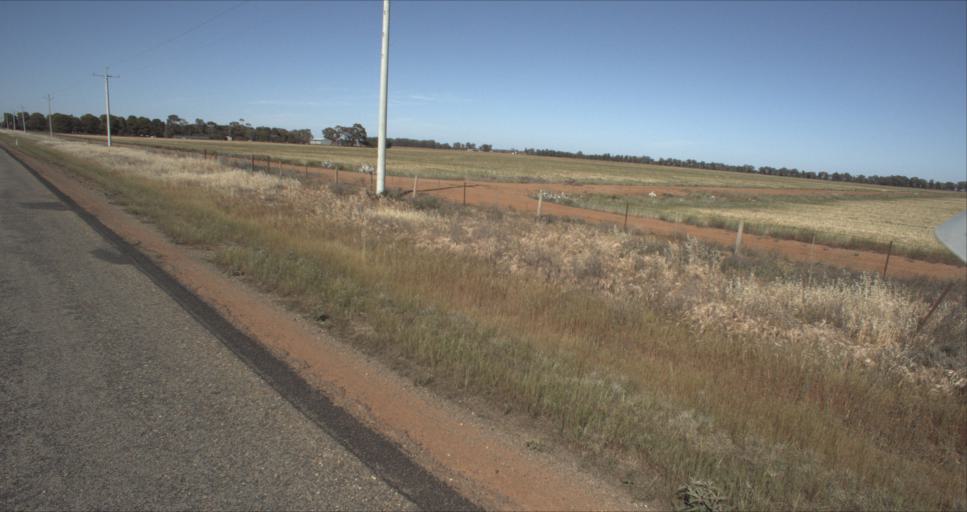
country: AU
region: New South Wales
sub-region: Leeton
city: Leeton
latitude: -34.5804
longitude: 146.2617
